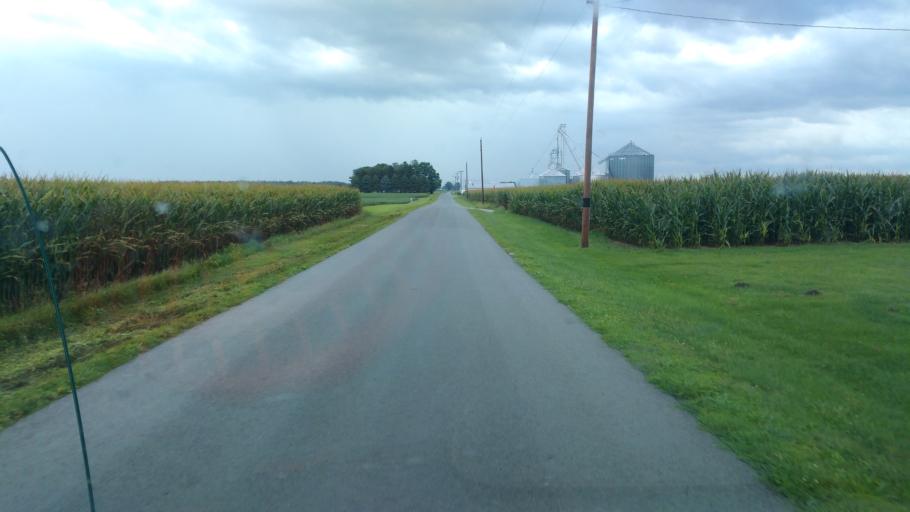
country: US
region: Ohio
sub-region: Hardin County
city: Kenton
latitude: 40.6894
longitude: -83.6322
